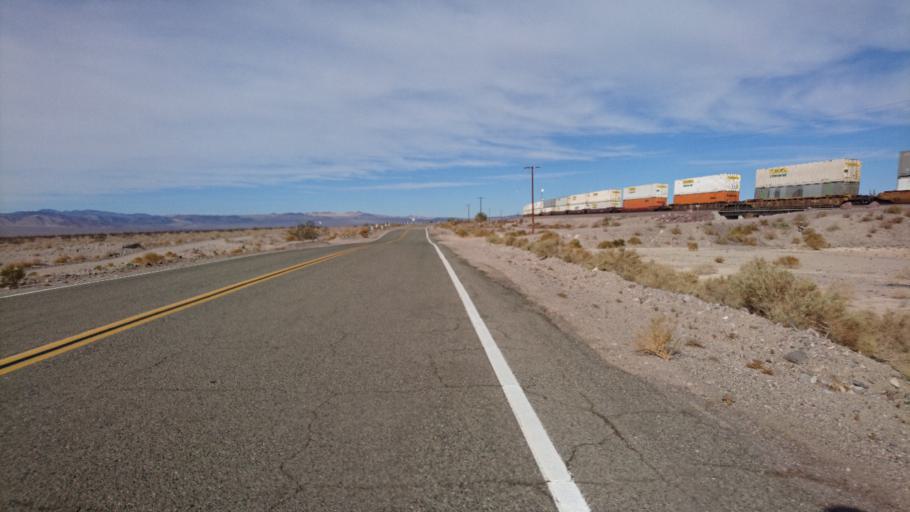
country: US
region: California
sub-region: San Bernardino County
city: Twentynine Palms
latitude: 34.6024
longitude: -115.9545
